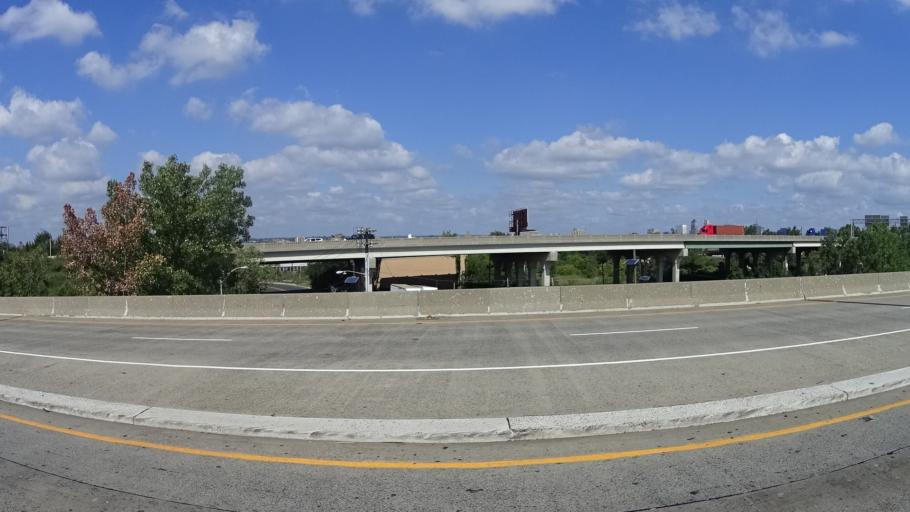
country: US
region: New Jersey
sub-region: Essex County
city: Newark
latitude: 40.7115
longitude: -74.1567
